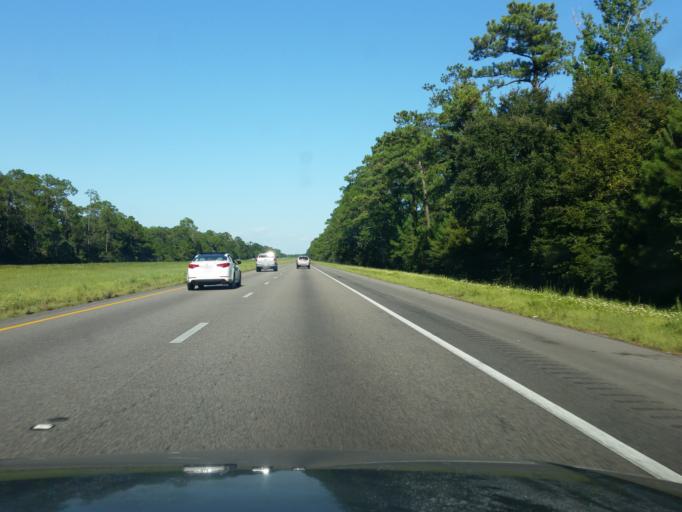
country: US
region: Mississippi
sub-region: Hancock County
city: Diamondhead
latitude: 30.3793
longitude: -89.3546
